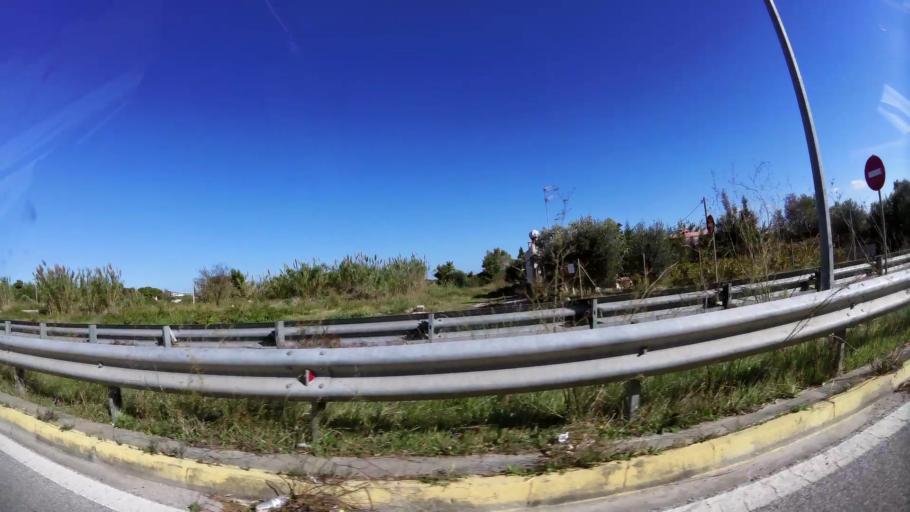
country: GR
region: Attica
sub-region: Nomarchia Anatolikis Attikis
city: Pallini
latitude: 38.0009
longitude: 23.8923
